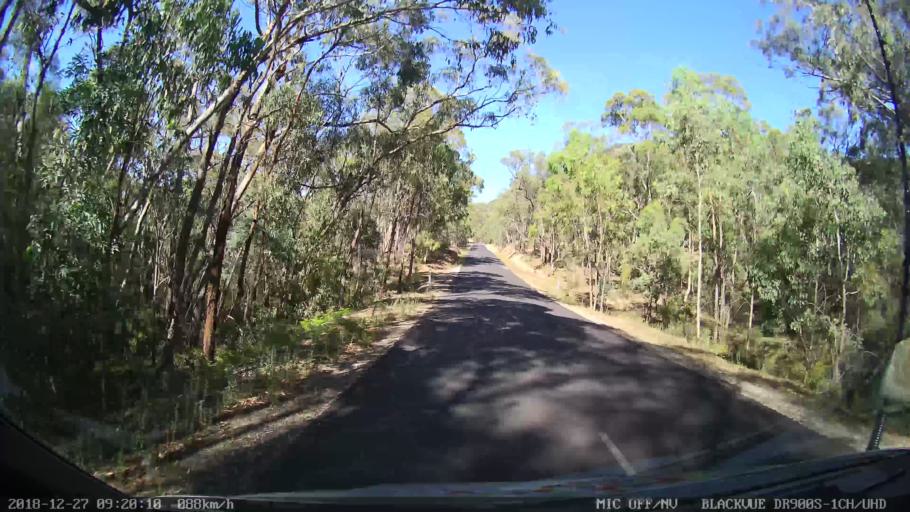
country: AU
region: New South Wales
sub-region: Lithgow
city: Portland
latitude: -33.1180
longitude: 150.0264
